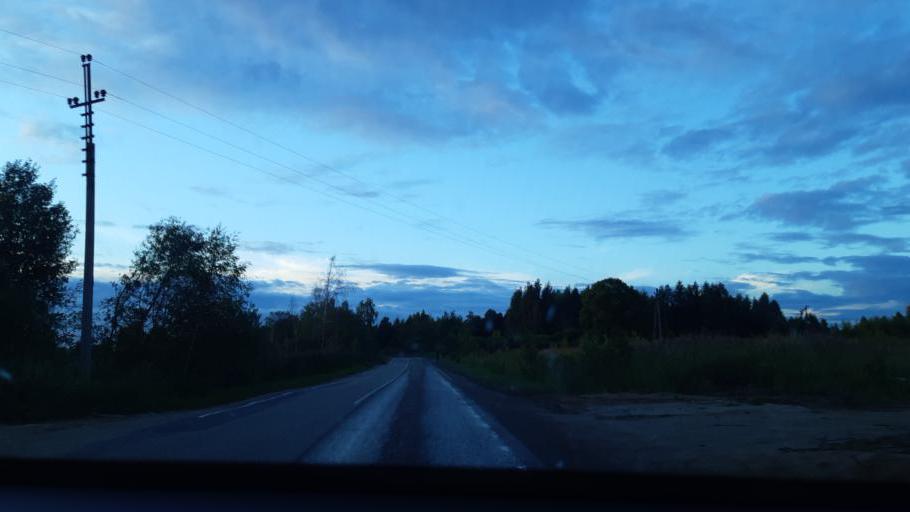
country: RU
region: Smolensk
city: Safonovo
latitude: 55.1280
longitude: 33.2003
